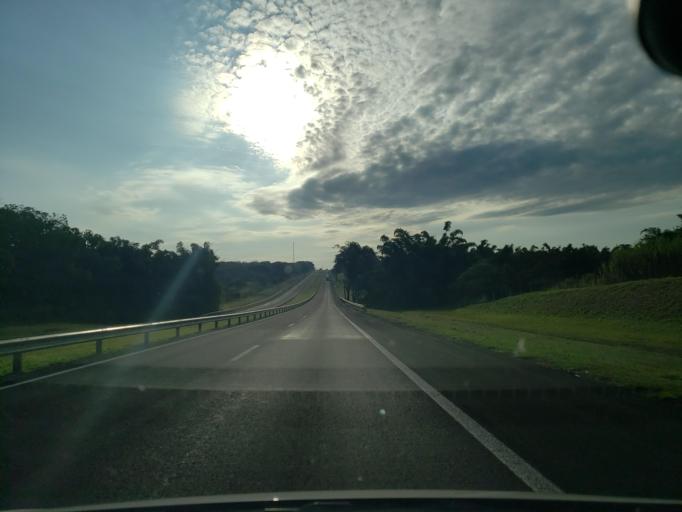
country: BR
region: Sao Paulo
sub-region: Valparaiso
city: Valparaiso
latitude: -21.1791
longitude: -50.9229
